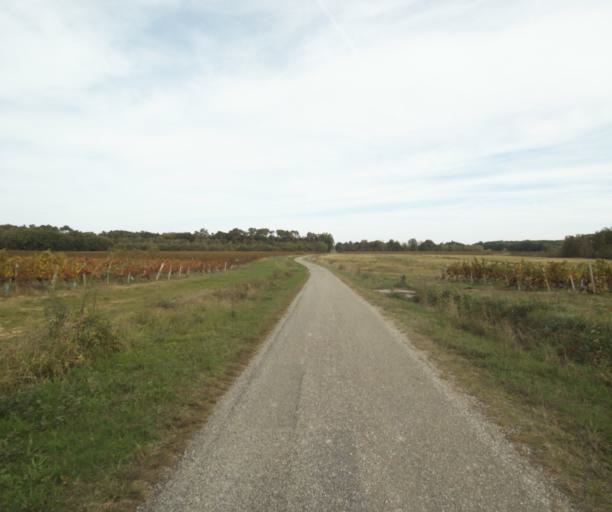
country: FR
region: Midi-Pyrenees
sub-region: Departement du Tarn-et-Garonne
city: Orgueil
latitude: 43.8834
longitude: 1.3920
